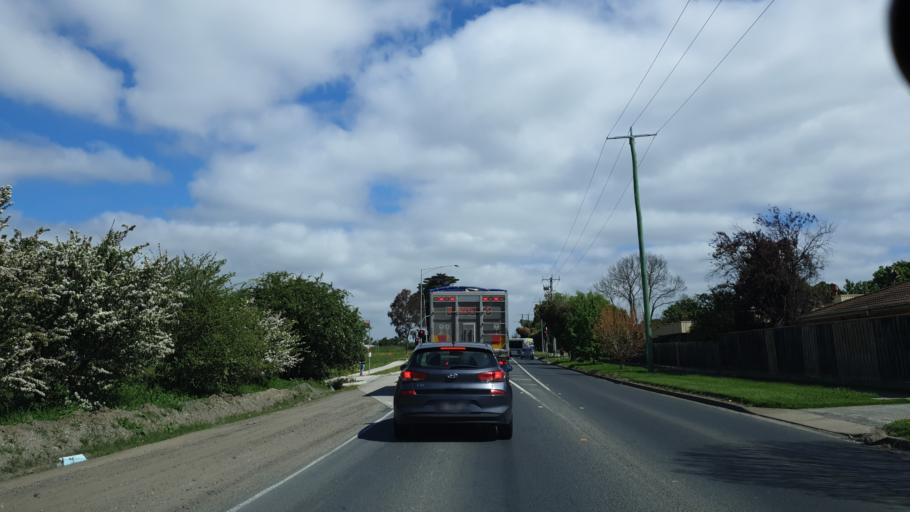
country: AU
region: Victoria
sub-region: Casey
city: Cranbourne
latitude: -38.1093
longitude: 145.2906
